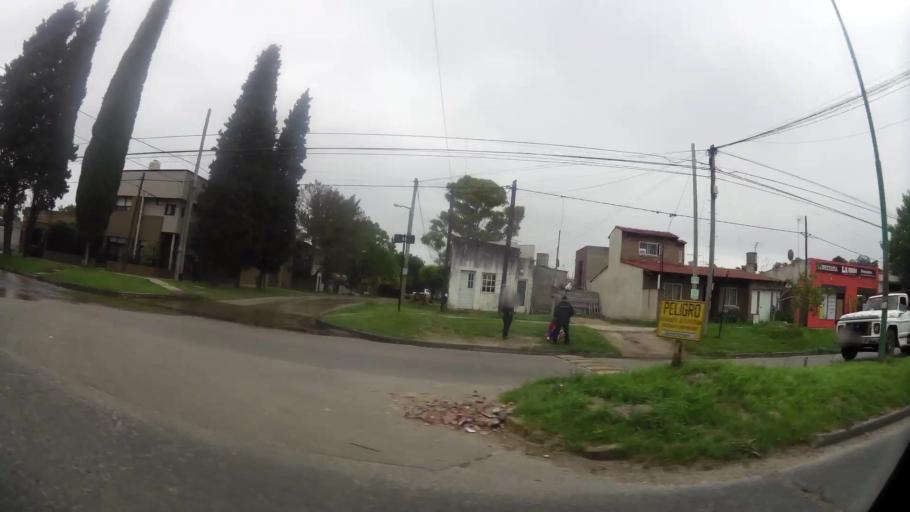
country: AR
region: Buenos Aires
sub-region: Partido de La Plata
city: La Plata
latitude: -34.9431
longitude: -57.9951
